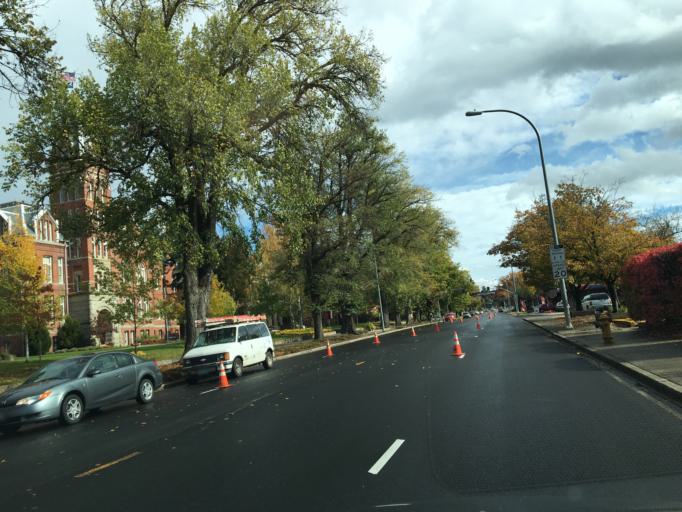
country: US
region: Washington
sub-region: Kittitas County
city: Ellensburg
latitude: 46.9997
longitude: -120.5431
